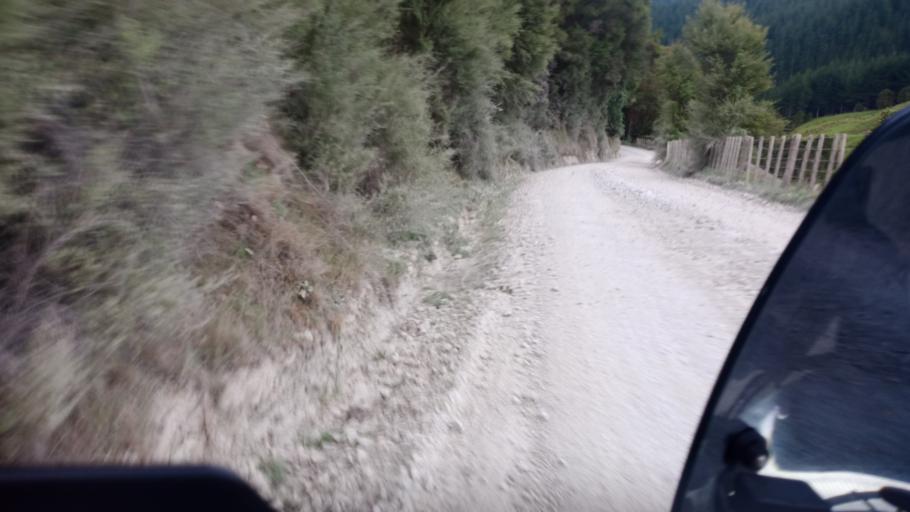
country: NZ
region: Gisborne
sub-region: Gisborne District
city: Gisborne
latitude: -38.4762
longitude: 177.9744
